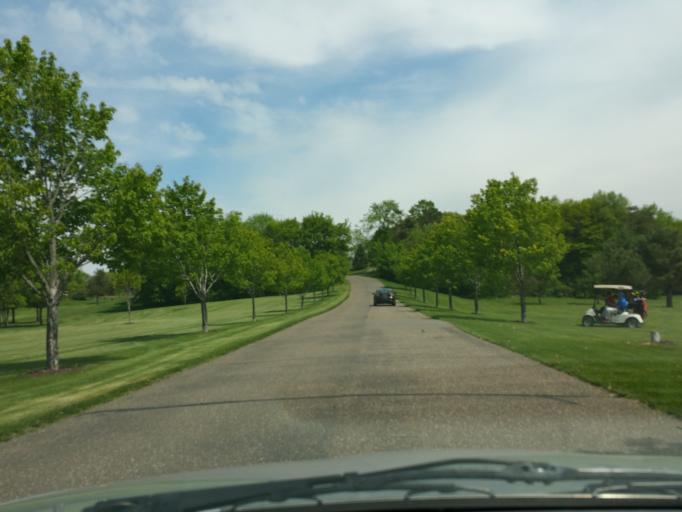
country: US
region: Wisconsin
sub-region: Pierce County
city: River Falls
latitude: 44.8876
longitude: -92.6464
